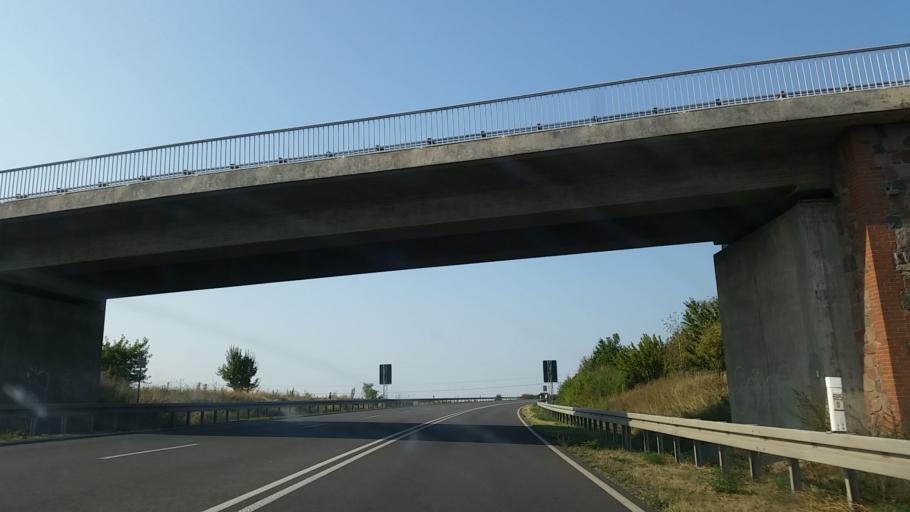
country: DE
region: Brandenburg
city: Pinnow
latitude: 53.0564
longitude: 14.0673
